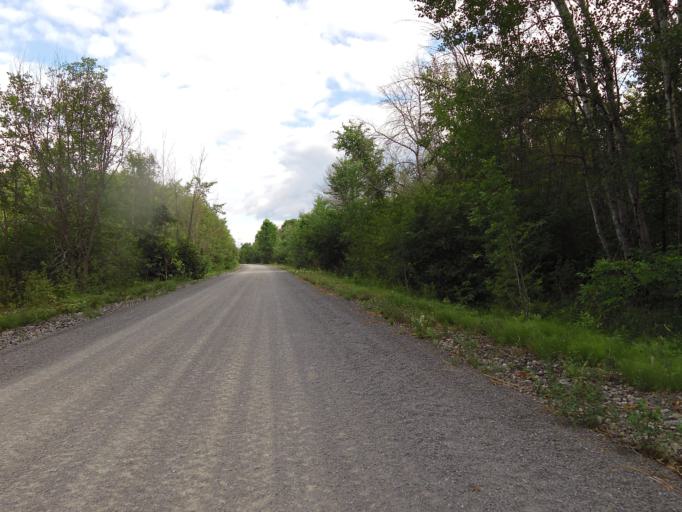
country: CA
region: Ontario
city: Arnprior
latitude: 45.2972
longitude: -76.2625
